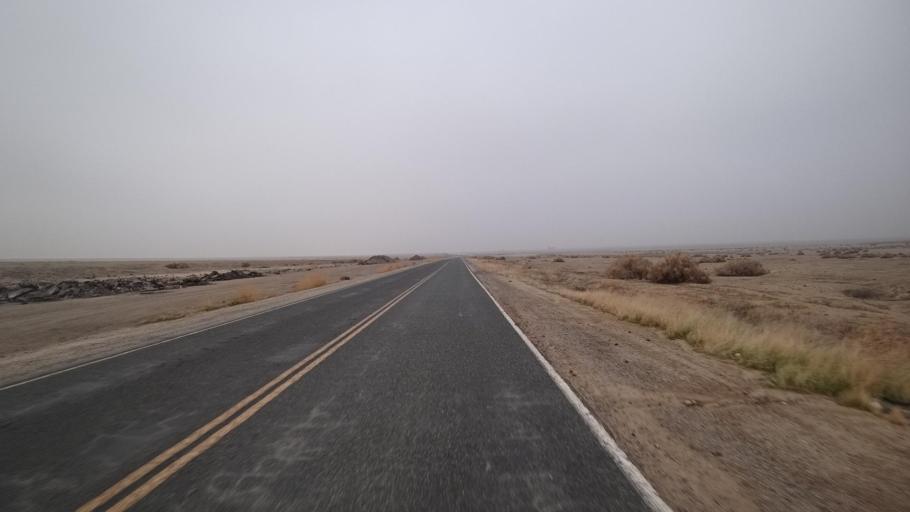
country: US
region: California
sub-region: Kern County
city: Buttonwillow
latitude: 35.3415
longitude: -119.4666
